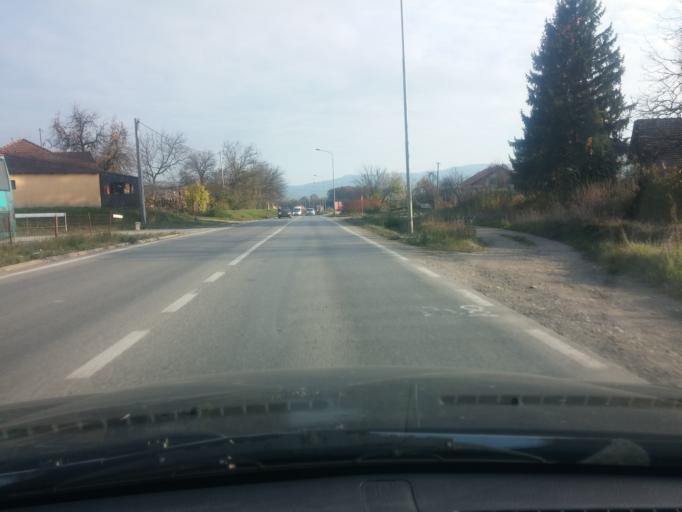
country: BA
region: Republika Srpska
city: Banja Luka
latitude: 44.8255
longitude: 17.1916
